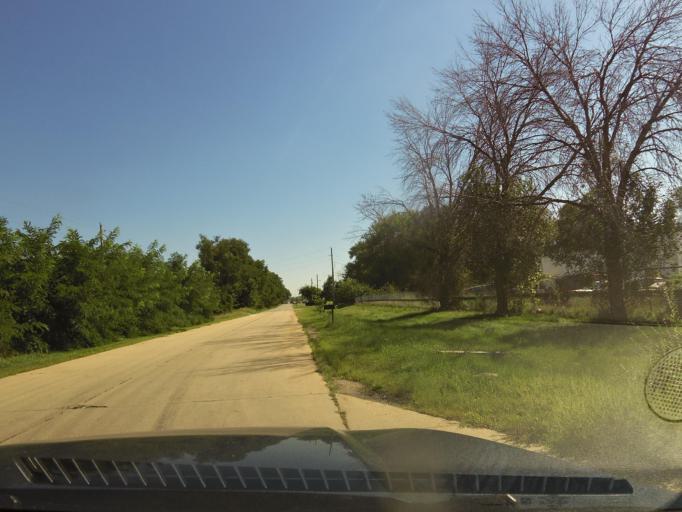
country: US
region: Iowa
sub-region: Black Hawk County
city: Waterloo
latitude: 42.4730
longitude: -92.3190
